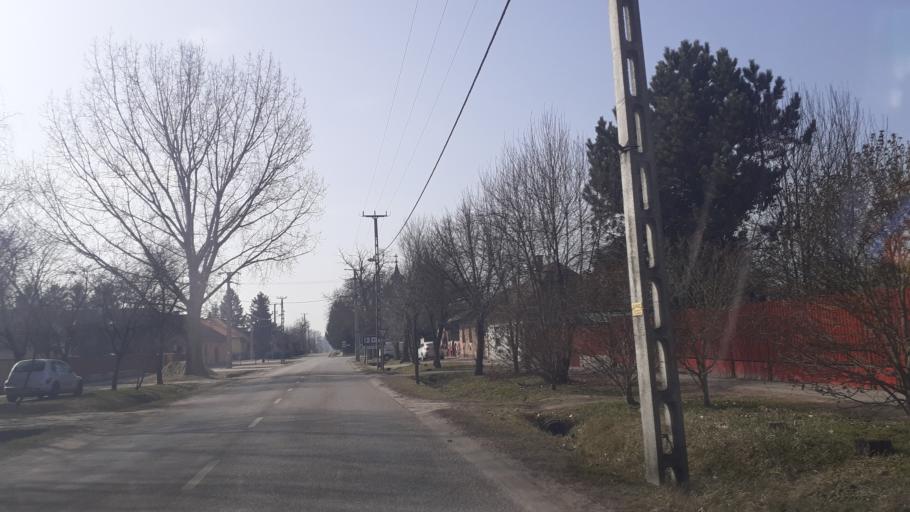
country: HU
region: Pest
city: Orkeny
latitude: 47.0823
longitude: 19.3714
